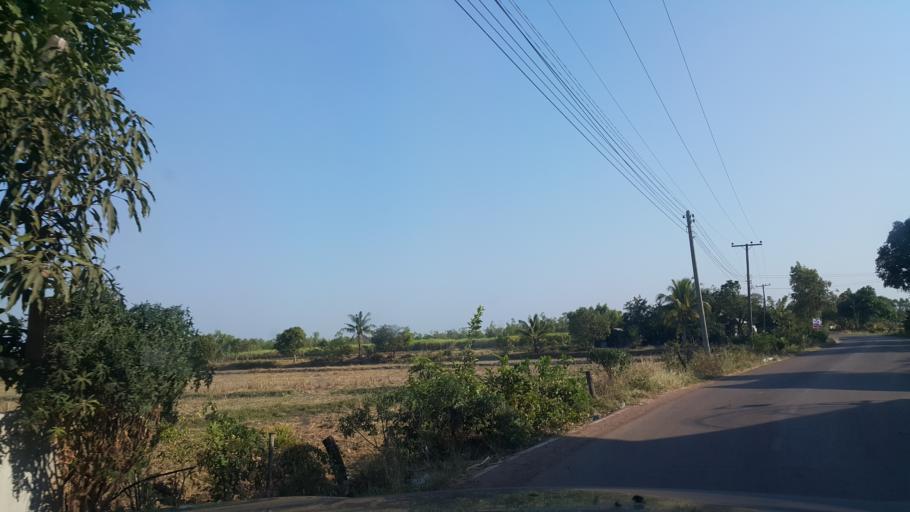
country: TH
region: Changwat Udon Thani
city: Ban Na Muang
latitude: 17.2387
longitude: 103.0684
